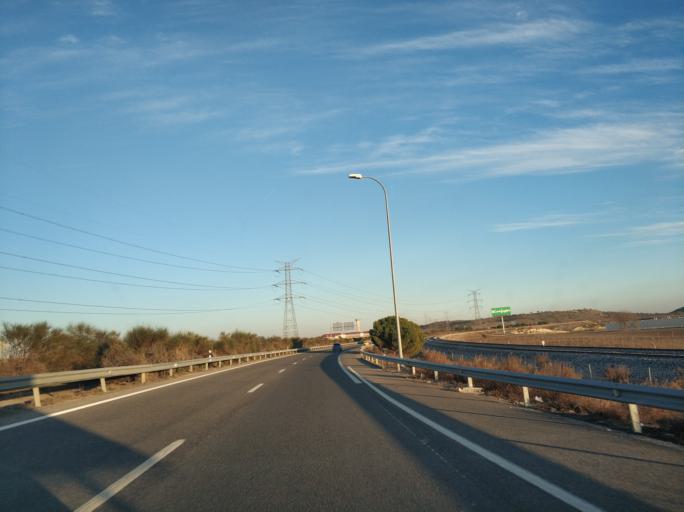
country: ES
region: Madrid
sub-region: Provincia de Madrid
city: Valdemoro
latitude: 40.2209
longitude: -3.6725
